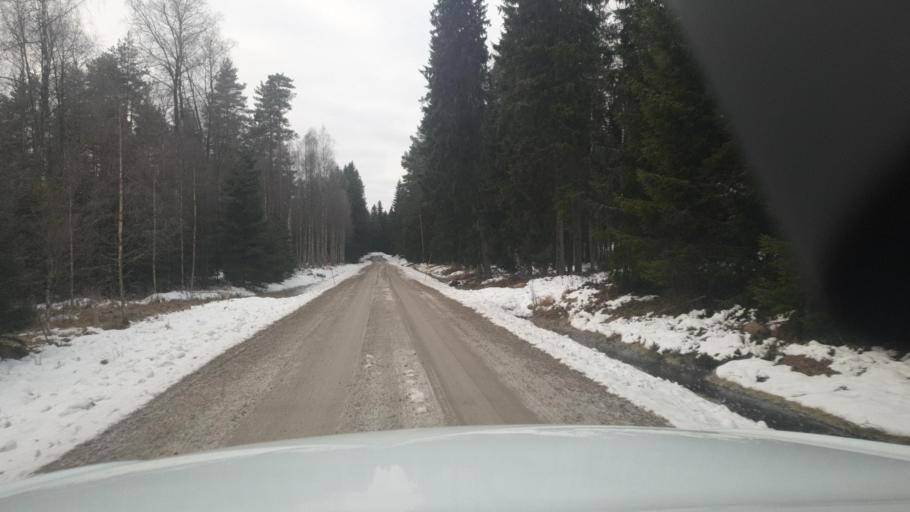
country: SE
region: Vaermland
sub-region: Sunne Kommun
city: Sunne
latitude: 59.8563
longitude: 12.8595
